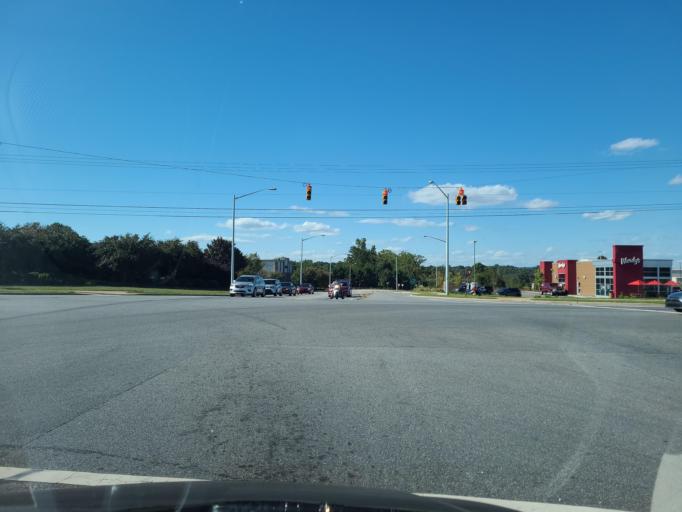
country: US
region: North Carolina
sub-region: Catawba County
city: Conover
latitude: 35.7259
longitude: -81.2072
